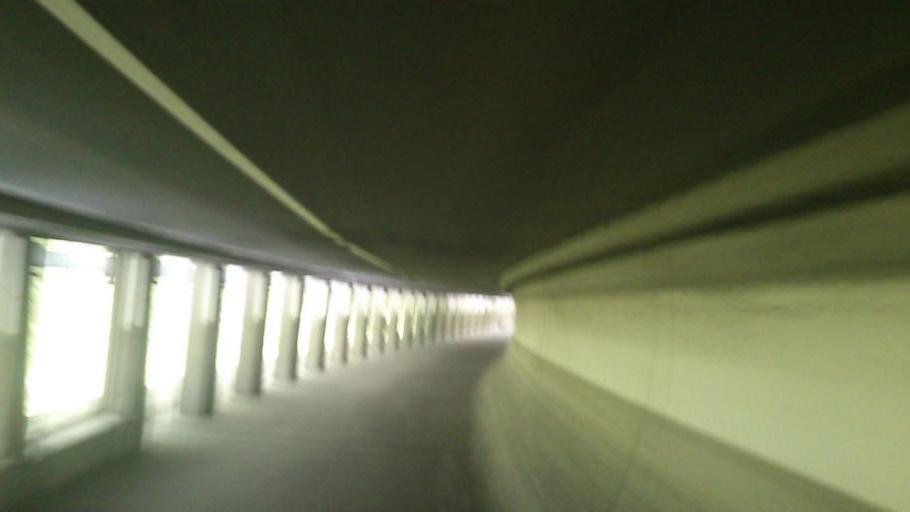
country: JP
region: Hokkaido
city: Kamikawa
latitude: 43.7429
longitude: 142.9353
